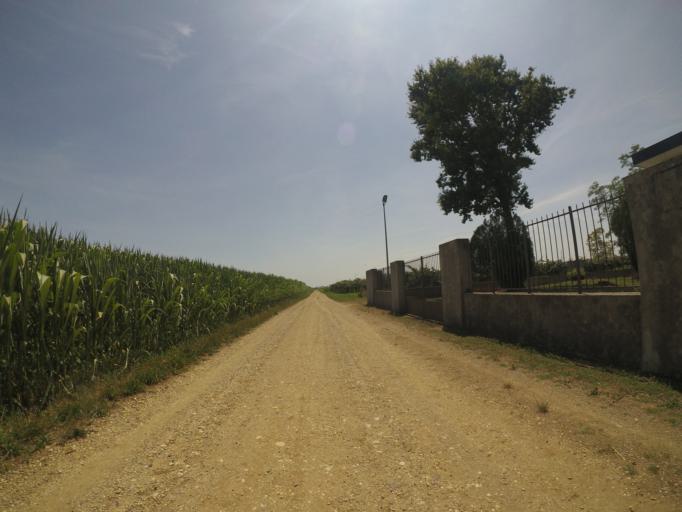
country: IT
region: Friuli Venezia Giulia
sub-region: Provincia di Udine
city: Bertiolo
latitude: 45.9728
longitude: 13.0954
